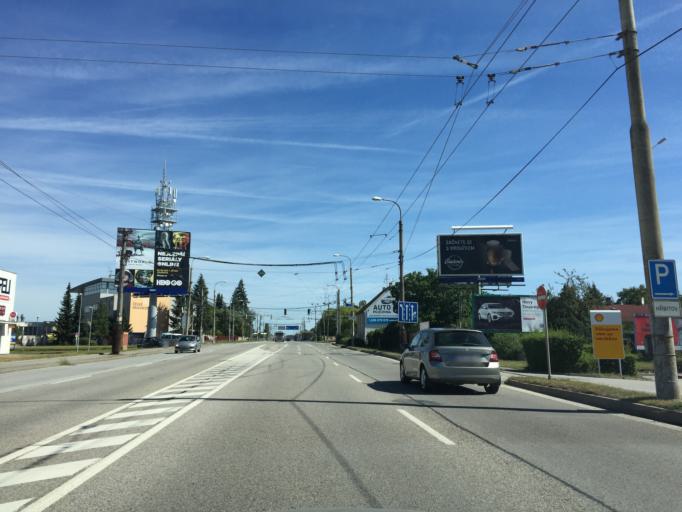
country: CZ
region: Jihocesky
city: Hrdejovice
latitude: 48.9976
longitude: 14.4807
